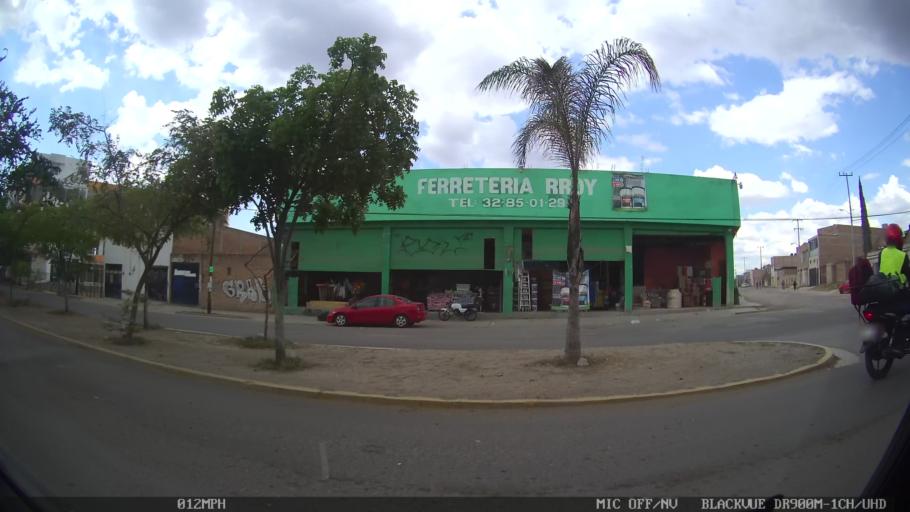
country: MX
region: Jalisco
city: Tlaquepaque
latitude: 20.6703
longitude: -103.2562
